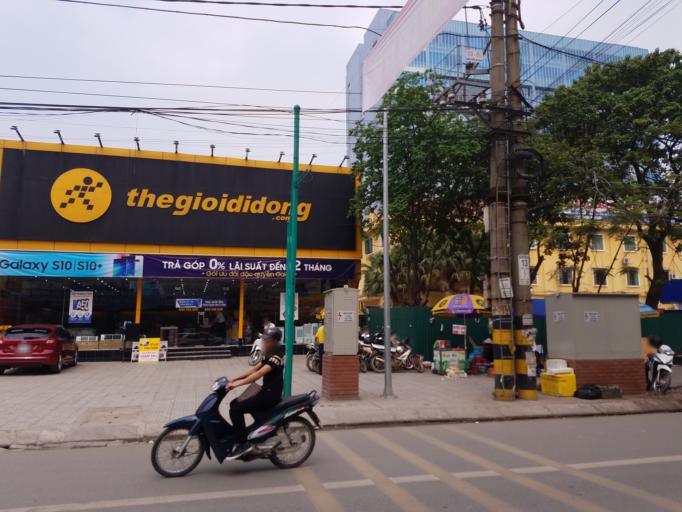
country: VN
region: Thai Nguyen
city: Thanh Pho Thai Nguyen
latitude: 21.5879
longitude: 105.8294
